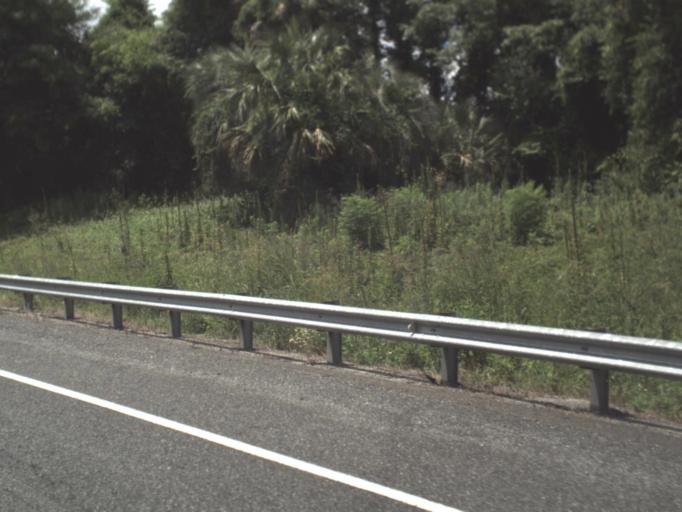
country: US
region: Florida
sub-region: Suwannee County
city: Wellborn
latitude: 30.2674
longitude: -82.7549
